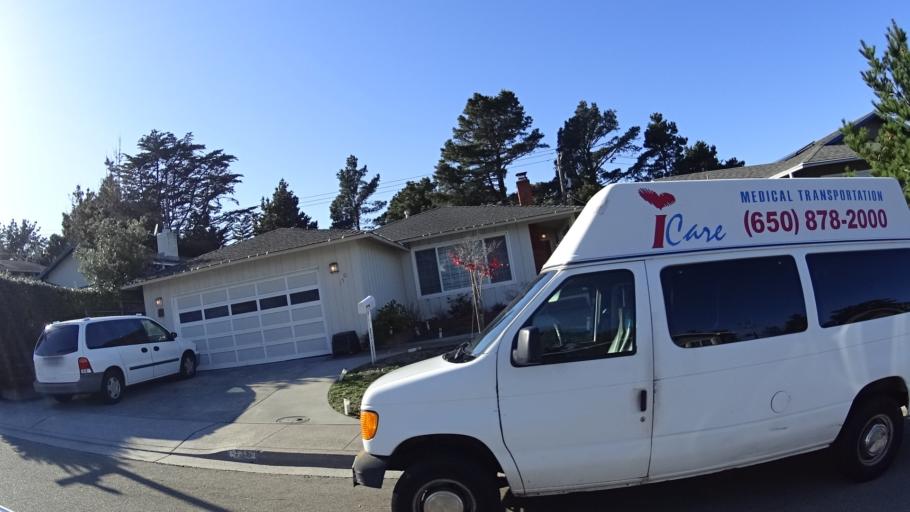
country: US
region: California
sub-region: San Mateo County
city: Pacifica
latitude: 37.6309
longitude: -122.4600
